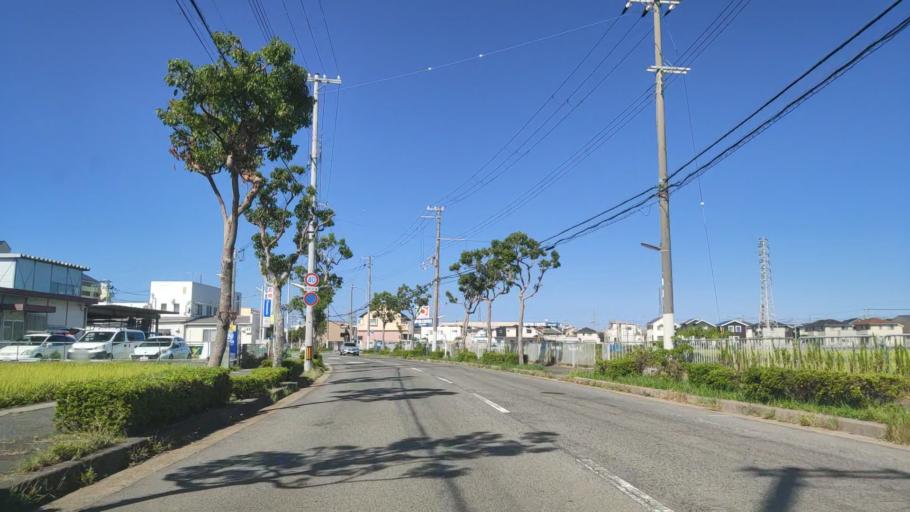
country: JP
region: Hyogo
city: Akashi
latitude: 34.6621
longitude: 134.9887
